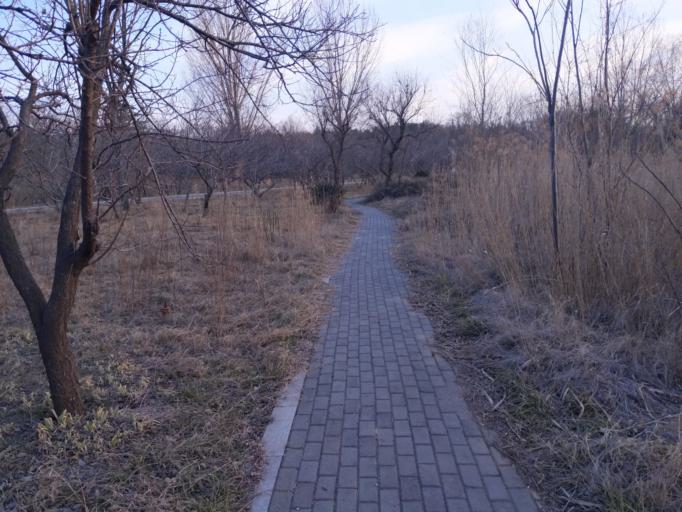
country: CN
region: Henan Sheng
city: Puyang
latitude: 35.7827
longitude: 114.9491
